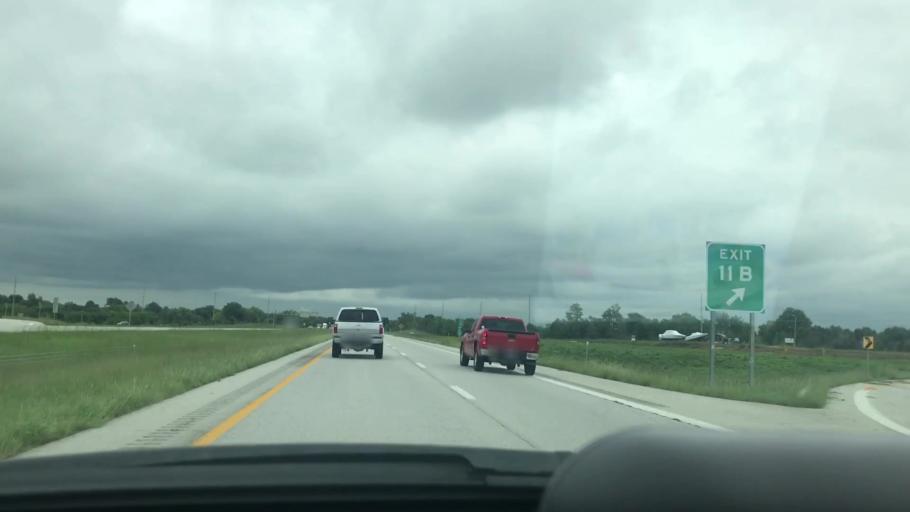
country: US
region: Missouri
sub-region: Jasper County
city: Duenweg
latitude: 37.0618
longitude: -94.4257
